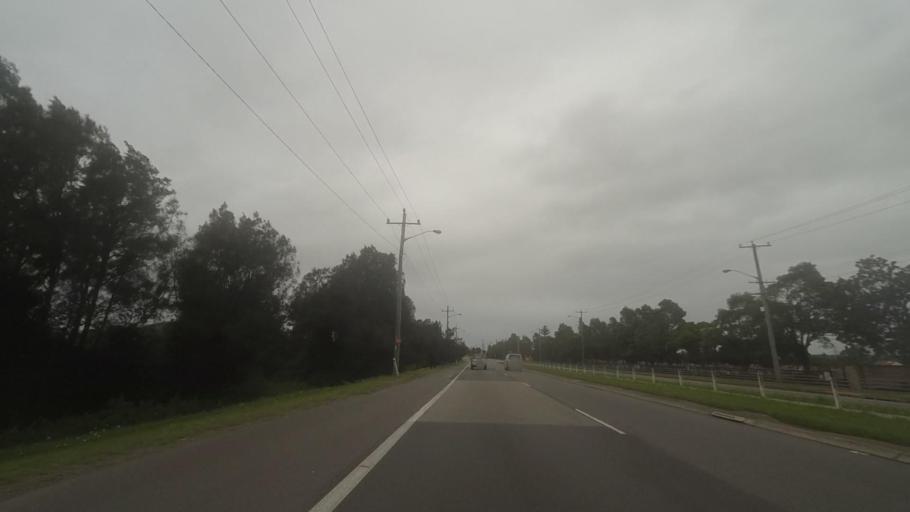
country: AU
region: New South Wales
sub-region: Newcastle
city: Mayfield West
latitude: -32.8662
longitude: 151.7075
